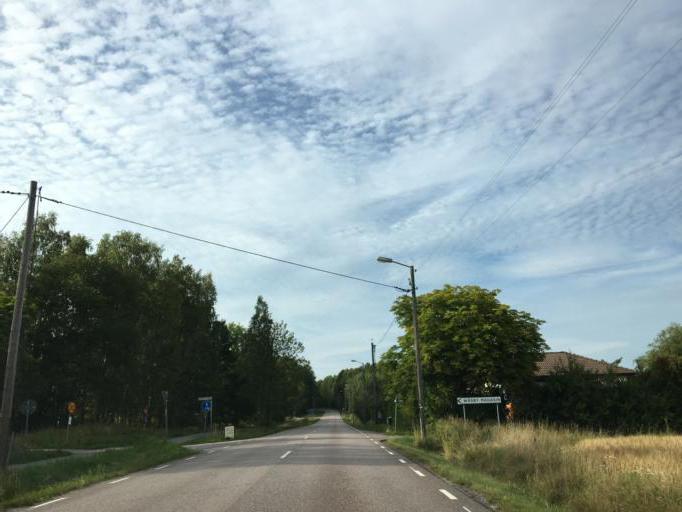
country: SE
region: Soedermanland
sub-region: Eskilstuna Kommun
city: Torshalla
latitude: 59.4444
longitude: 16.4510
